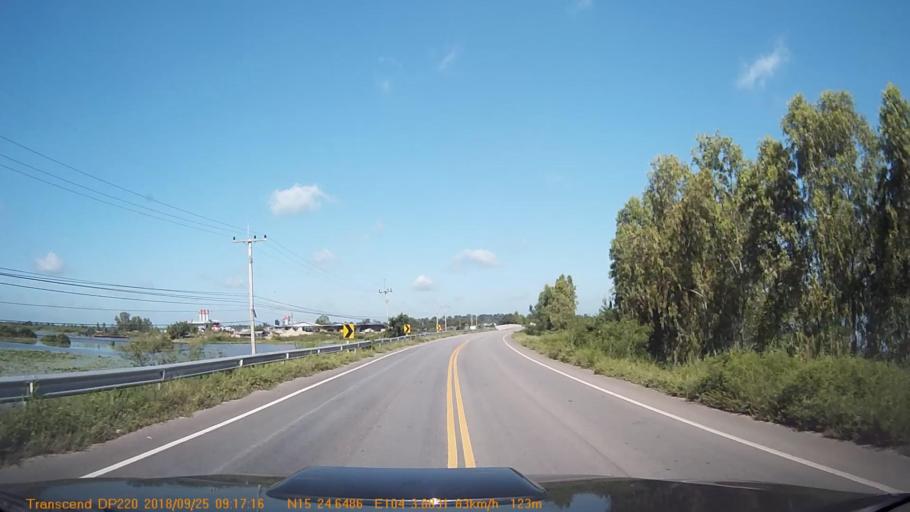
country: TH
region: Sisaket
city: Sila Lat
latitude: 15.4108
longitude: 104.0647
